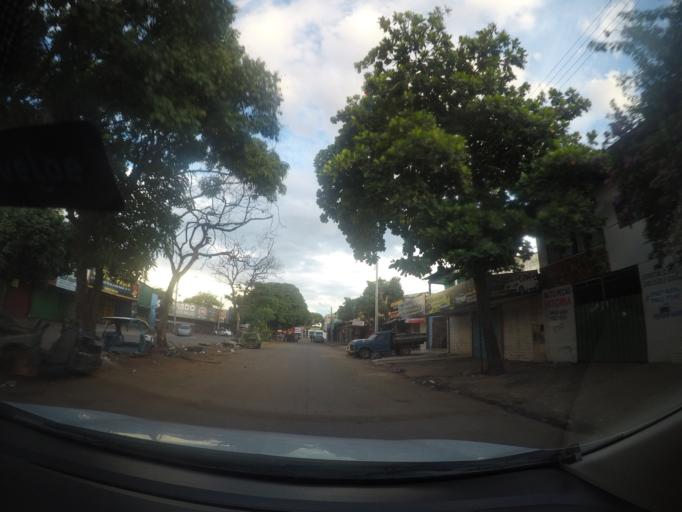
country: BR
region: Goias
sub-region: Goiania
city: Goiania
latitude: -16.6909
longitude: -49.3170
